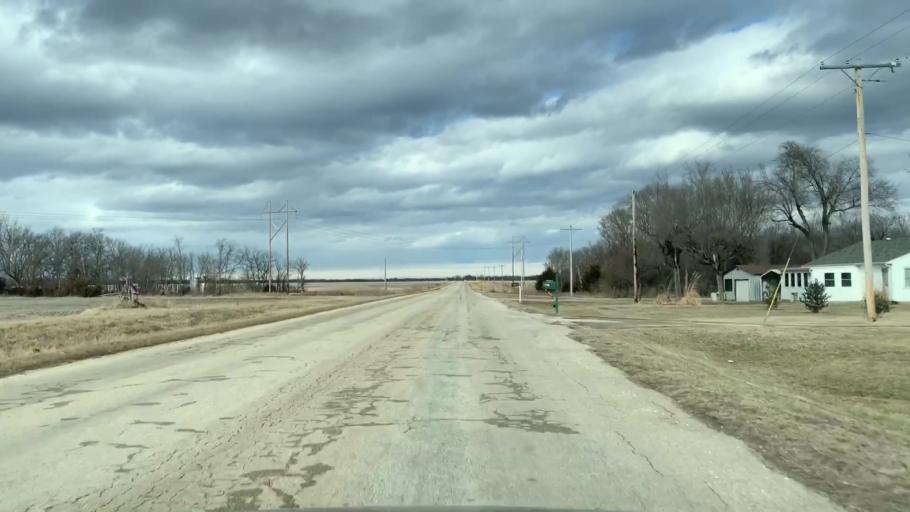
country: US
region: Kansas
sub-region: Allen County
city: Humboldt
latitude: 37.7678
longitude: -95.4706
